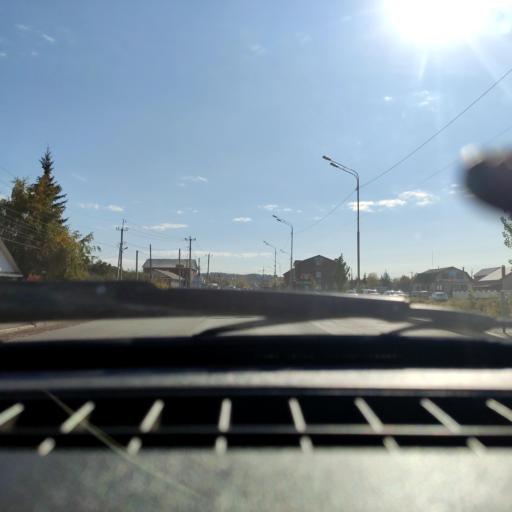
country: RU
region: Bashkortostan
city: Ufa
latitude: 54.6143
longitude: 55.9356
